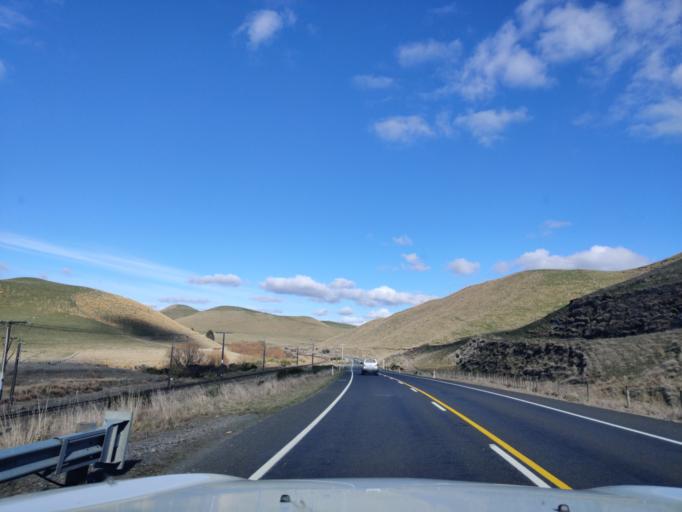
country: NZ
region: Manawatu-Wanganui
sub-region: Ruapehu District
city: Waiouru
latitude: -39.5012
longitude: 175.6738
